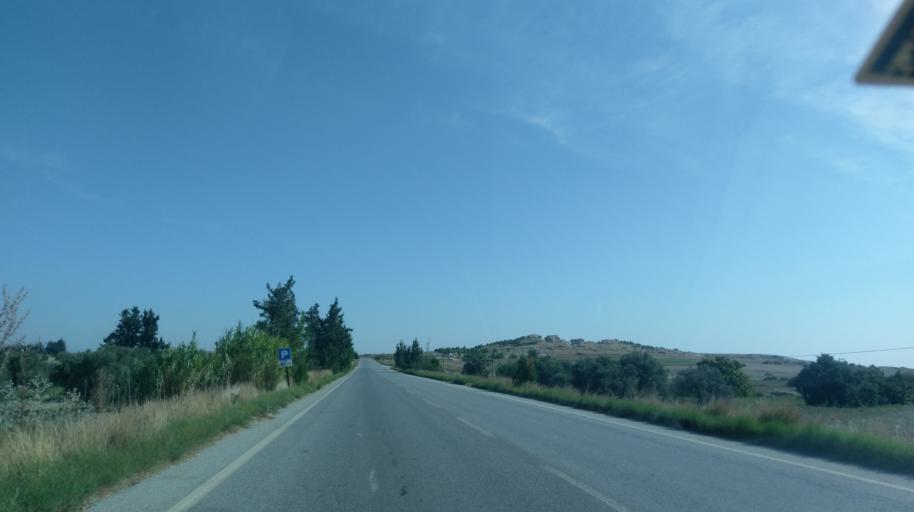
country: CY
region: Ammochostos
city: Lefkonoiko
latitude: 35.2506
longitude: 33.6217
